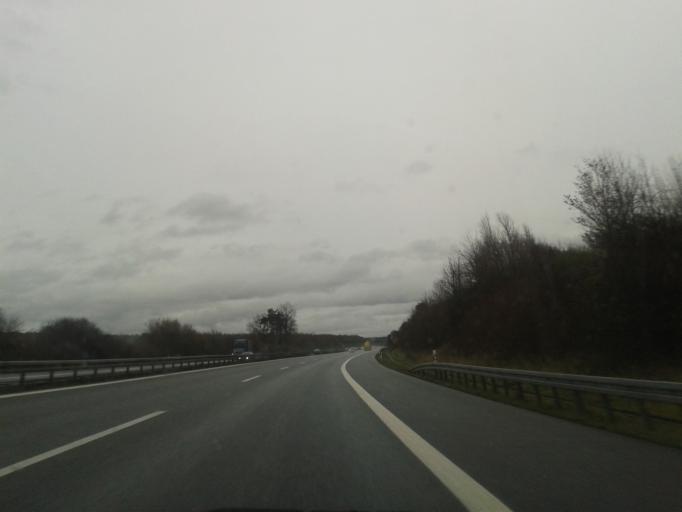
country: DE
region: Saxony
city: Lichtenberg
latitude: 51.1601
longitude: 13.9658
